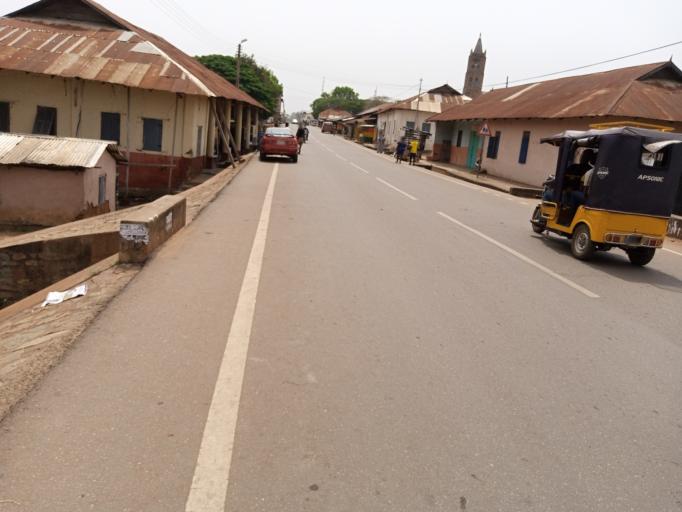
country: GH
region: Volta
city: Kpandu
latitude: 6.9993
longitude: 0.2944
